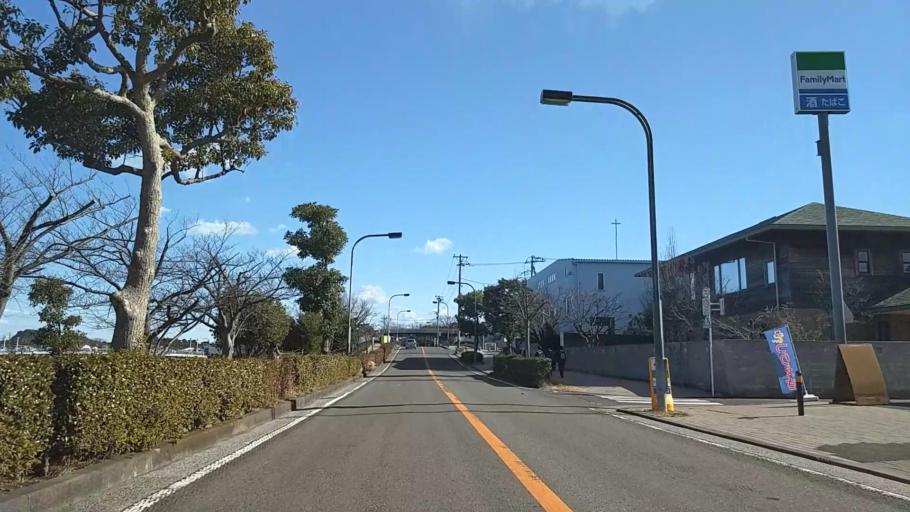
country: JP
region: Kanagawa
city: Yokosuka
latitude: 35.3269
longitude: 139.6279
